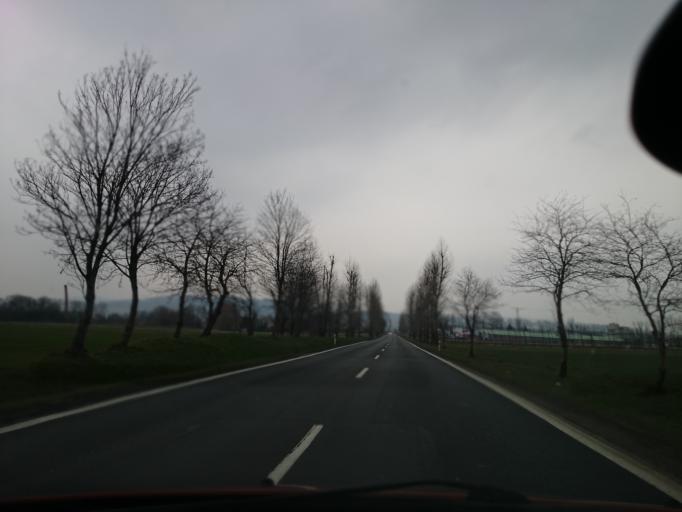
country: PL
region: Lower Silesian Voivodeship
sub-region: Powiat klodzki
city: Klodzko
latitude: 50.4416
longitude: 16.6275
